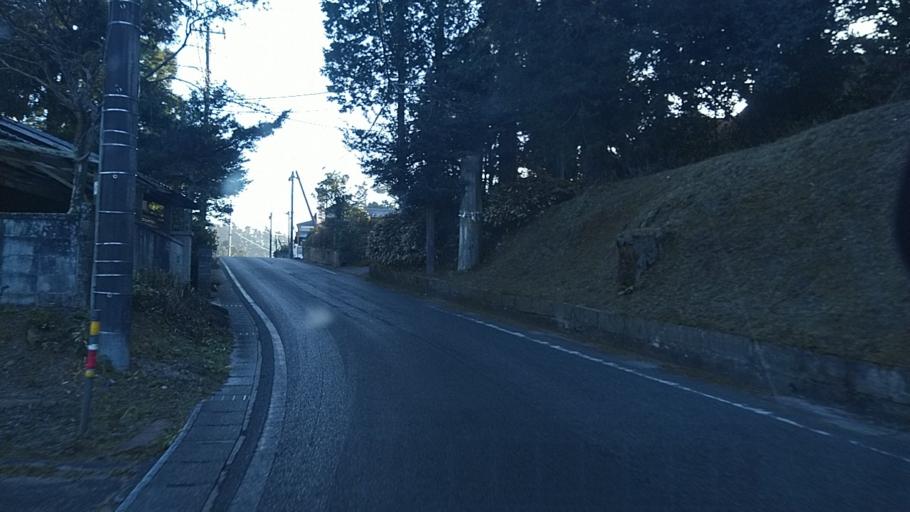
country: JP
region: Chiba
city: Kimitsu
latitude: 35.2548
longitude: 139.9586
